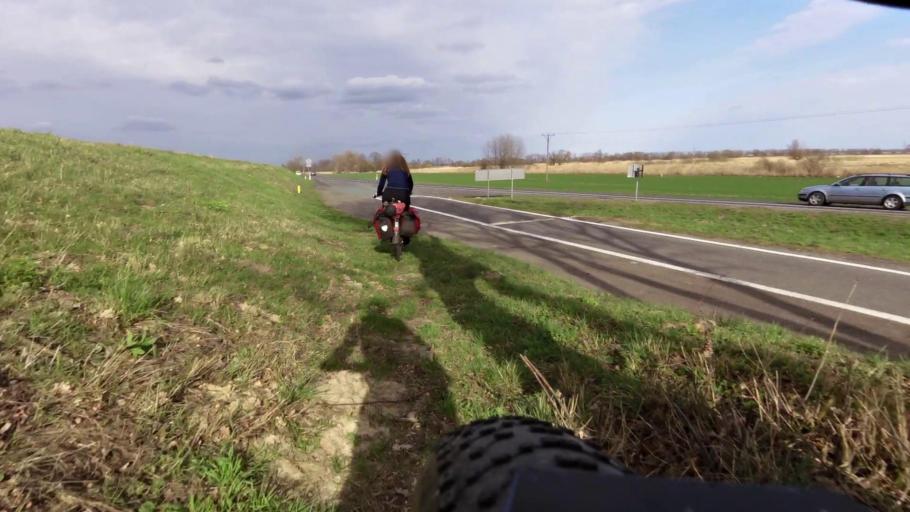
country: PL
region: Lubusz
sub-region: Powiat gorzowski
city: Kostrzyn nad Odra
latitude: 52.5609
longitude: 14.6331
